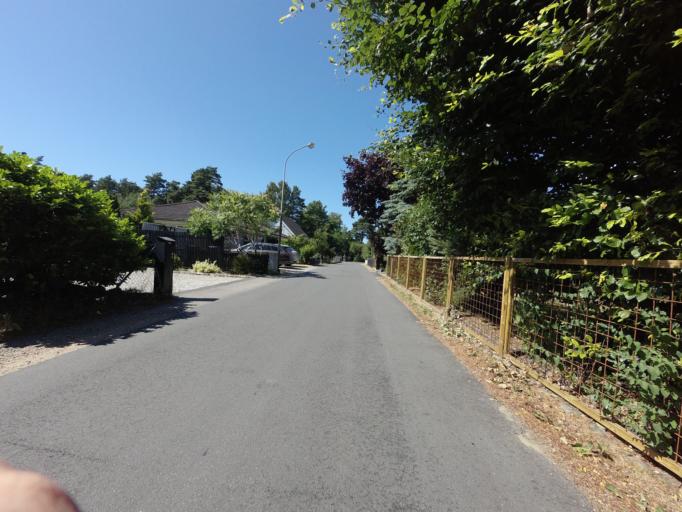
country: SE
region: Skane
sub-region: Vellinge Kommun
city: Hollviken
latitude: 55.4112
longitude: 12.9477
